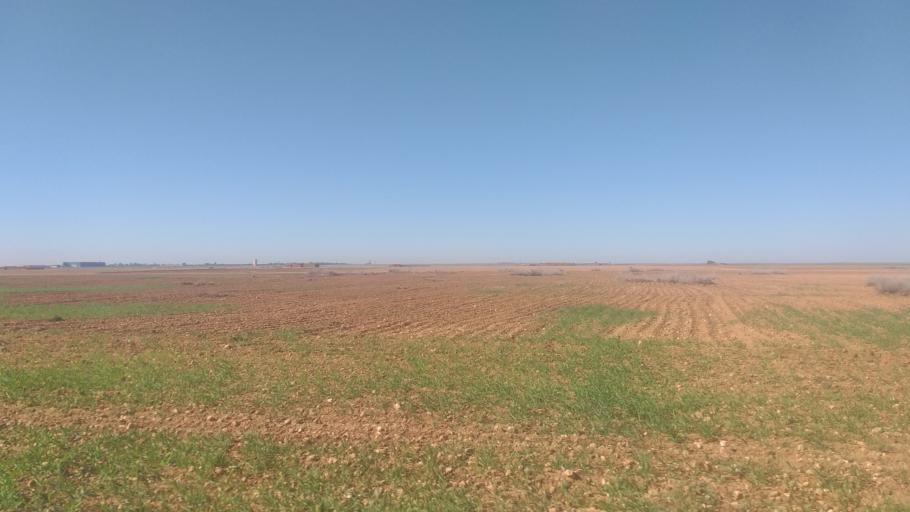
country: MA
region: Marrakech-Tensift-Al Haouz
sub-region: Kelaa-Des-Sraghna
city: Sidi Bou Othmane
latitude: 32.1456
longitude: -7.8599
